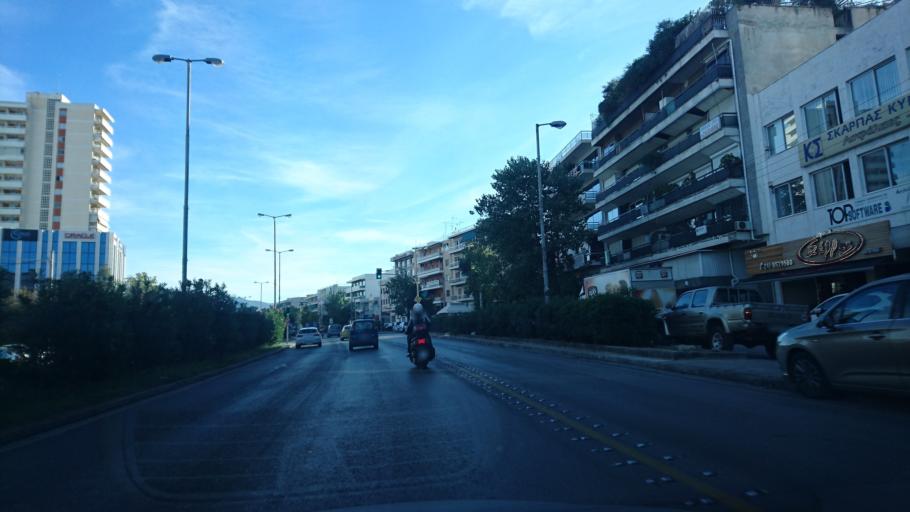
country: GR
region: Attica
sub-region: Nomarchia Athinas
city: Neo Psychiko
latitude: 38.0021
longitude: 23.7906
